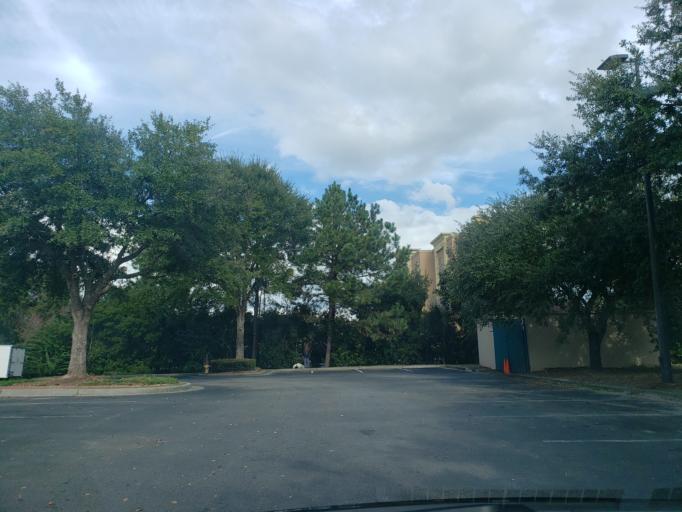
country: US
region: Georgia
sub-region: Chatham County
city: Georgetown
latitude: 32.0055
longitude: -81.2775
